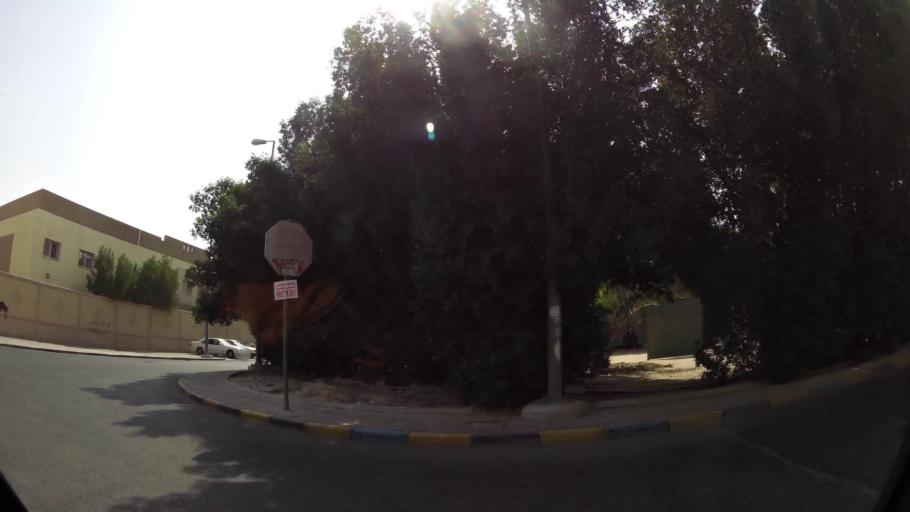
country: KW
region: Muhafazat al Jahra'
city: Al Jahra'
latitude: 29.3025
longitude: 47.7135
